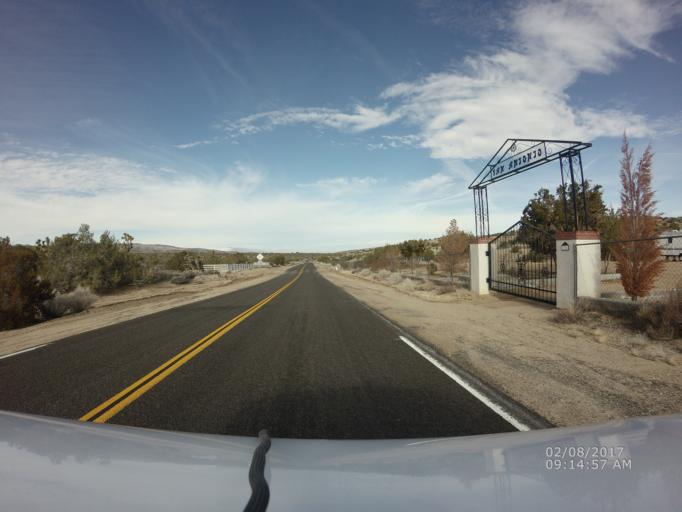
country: US
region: California
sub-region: Los Angeles County
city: Littlerock
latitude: 34.4688
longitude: -117.8929
